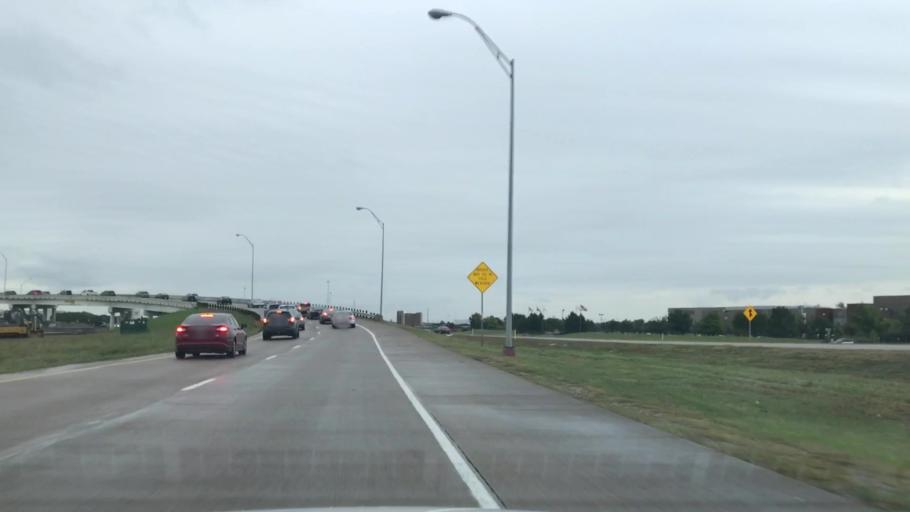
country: US
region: Texas
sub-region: Dallas County
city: Coppell
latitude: 32.9627
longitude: -97.0377
